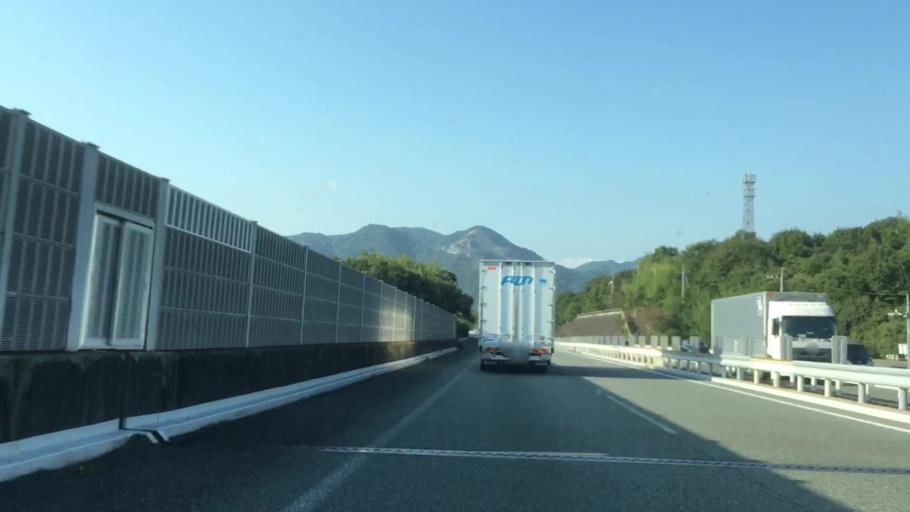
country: JP
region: Yamaguchi
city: Hofu
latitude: 34.0625
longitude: 131.5021
